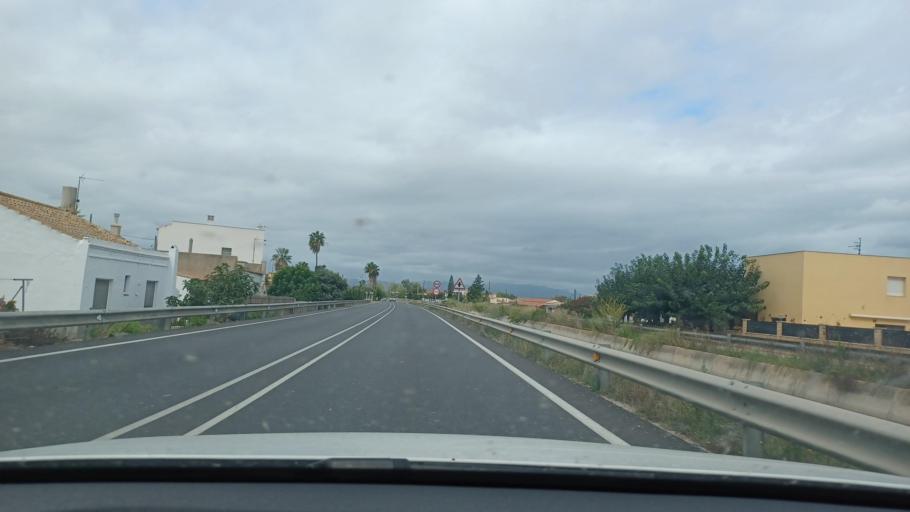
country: ES
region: Catalonia
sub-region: Provincia de Tarragona
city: Deltebre
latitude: 40.7169
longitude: 0.7510
